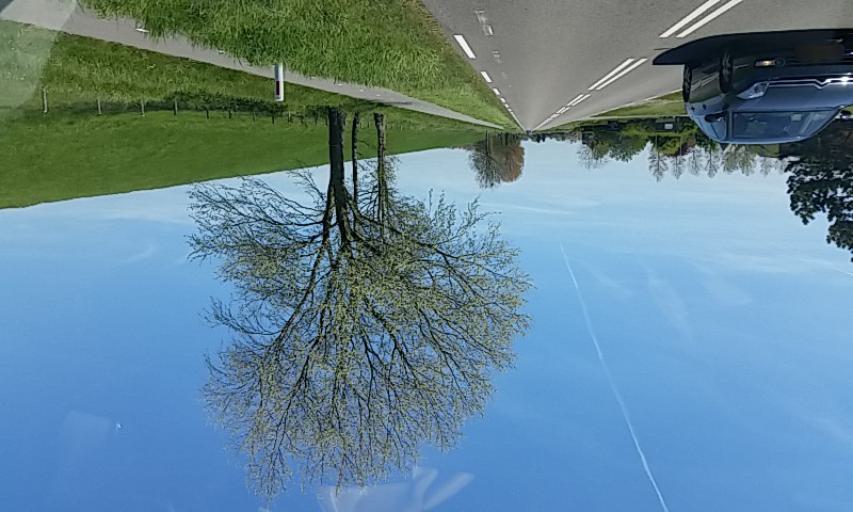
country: NL
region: Zeeland
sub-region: Gemeente Vlissingen
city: Vlissingen
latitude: 51.3765
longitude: 3.6267
